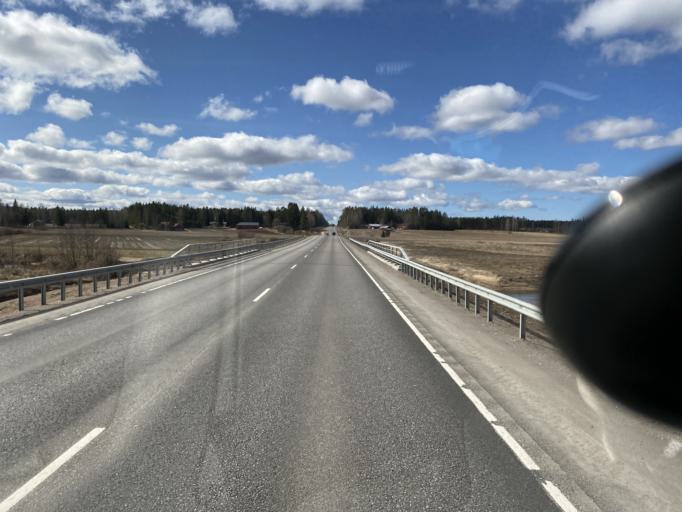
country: FI
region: Satakunta
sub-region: Rauma
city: Koeylioe
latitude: 61.1541
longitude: 22.2658
